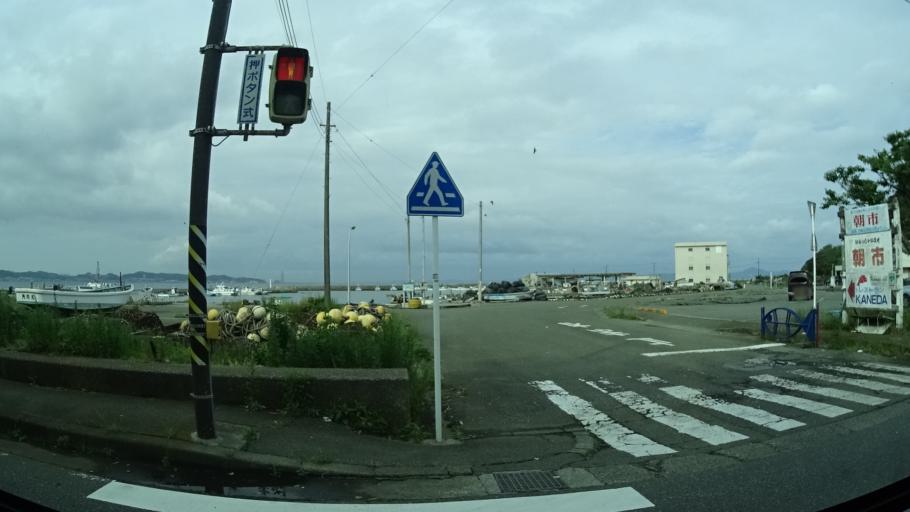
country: JP
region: Kanagawa
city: Miura
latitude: 35.1585
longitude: 139.6639
